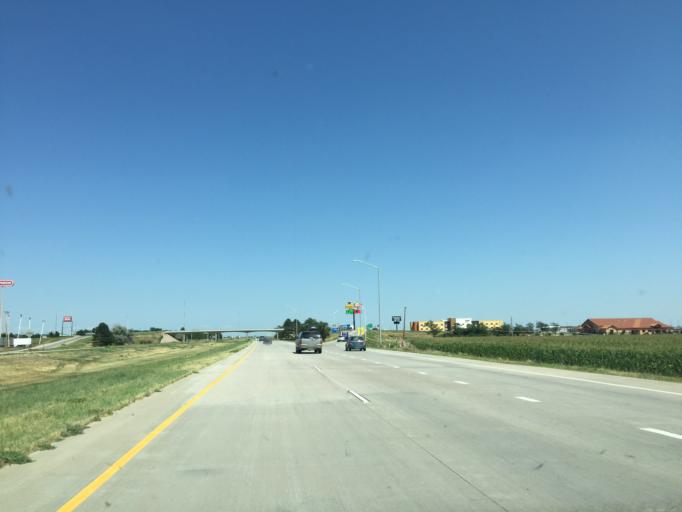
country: US
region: Colorado
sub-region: Kit Carson County
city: Burlington
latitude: 39.2939
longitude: -102.2832
